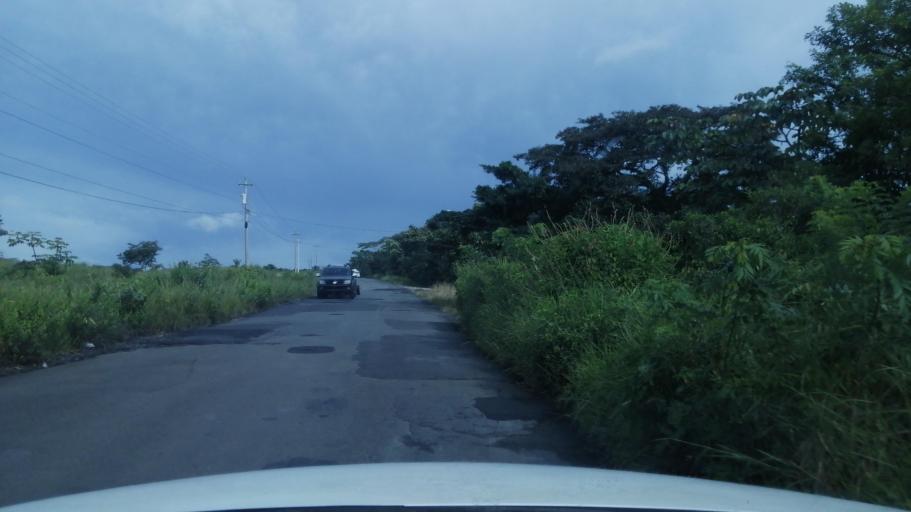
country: PA
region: Chiriqui
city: Potrerillos Abajo
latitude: 8.6705
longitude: -82.4342
